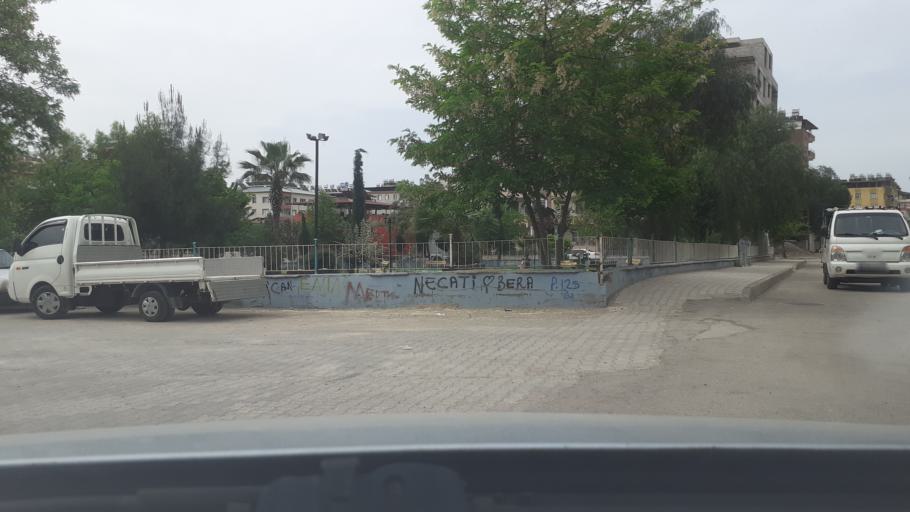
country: TR
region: Hatay
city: Kirikhan
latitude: 36.4928
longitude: 36.3668
